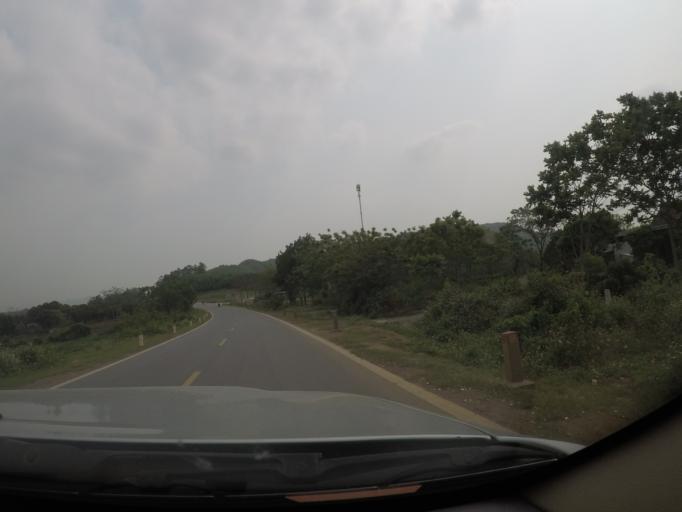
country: VN
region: Thanh Hoa
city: Thi Tran Ben Sung
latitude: 19.3939
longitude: 105.4548
